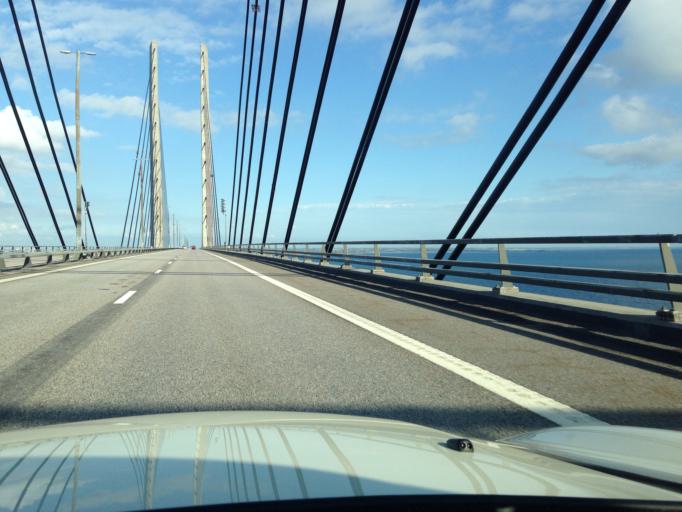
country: SE
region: Skane
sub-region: Malmo
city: Bunkeflostrand
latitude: 55.5758
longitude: 12.8240
